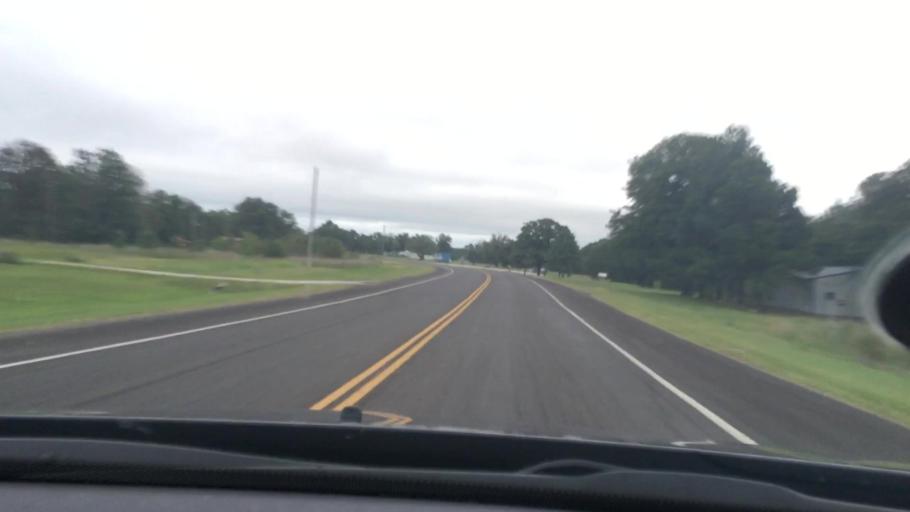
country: US
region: Oklahoma
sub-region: Sequoyah County
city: Vian
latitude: 35.5580
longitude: -94.9796
